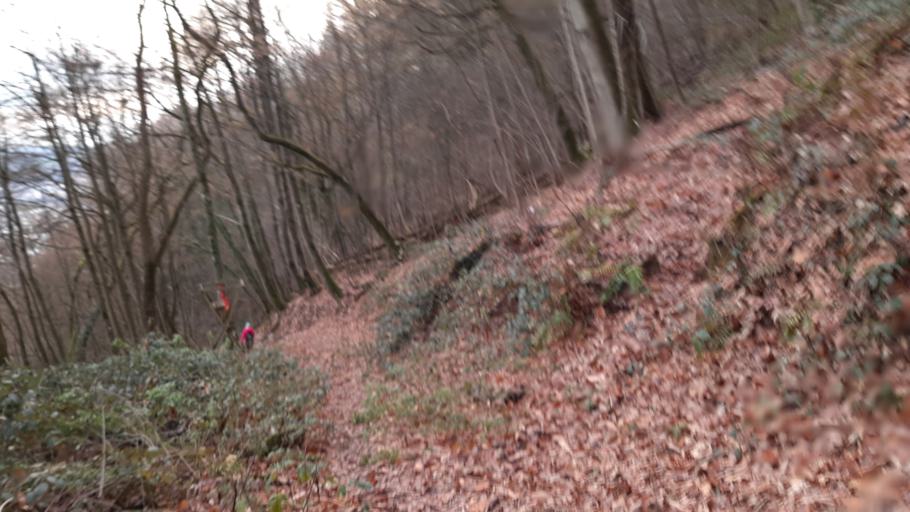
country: DE
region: Rheinland-Pfalz
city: Trier
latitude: 49.7558
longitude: 6.6148
